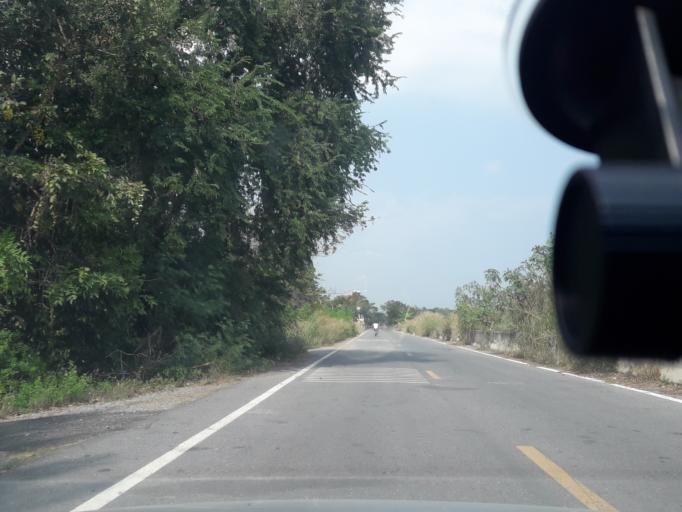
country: TH
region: Sara Buri
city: Nong Khae
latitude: 14.2725
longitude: 100.8912
